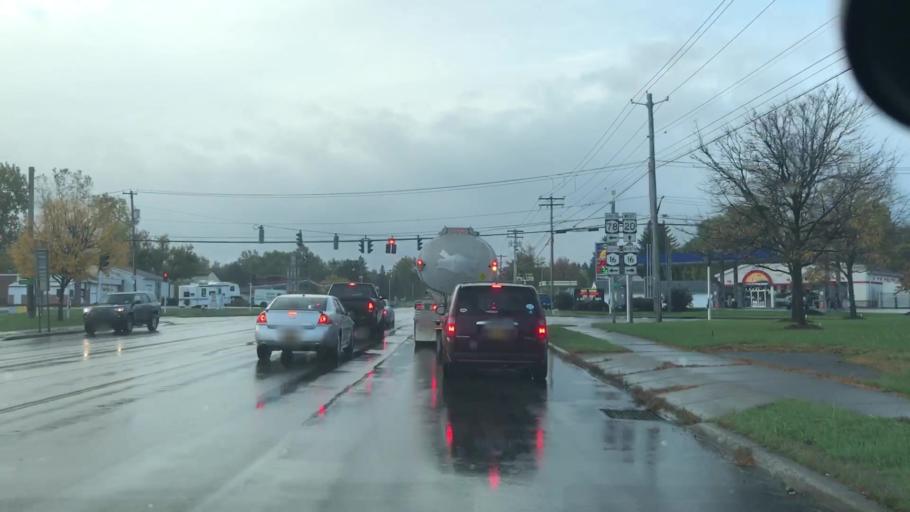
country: US
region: New York
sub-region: Erie County
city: Elma Center
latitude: 42.8280
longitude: -78.6970
